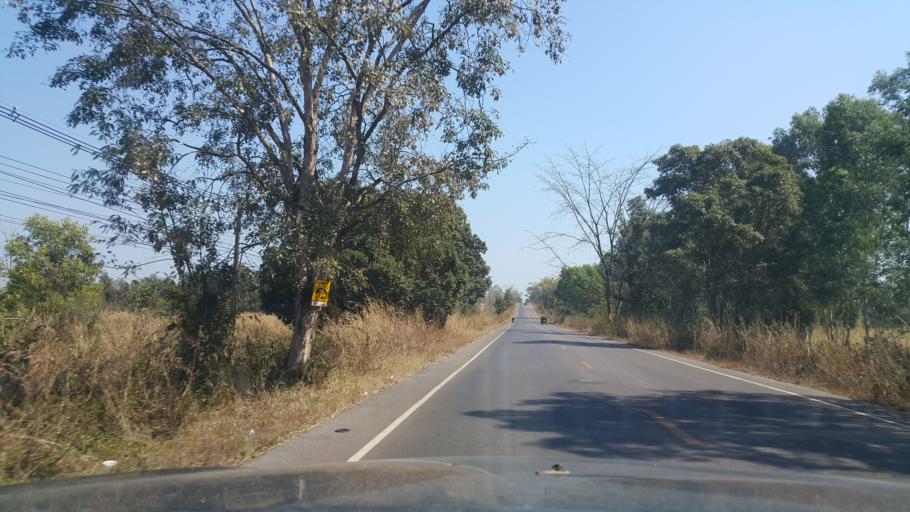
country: TH
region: Changwat Udon Thani
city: Ban Dung
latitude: 17.6085
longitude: 103.2666
